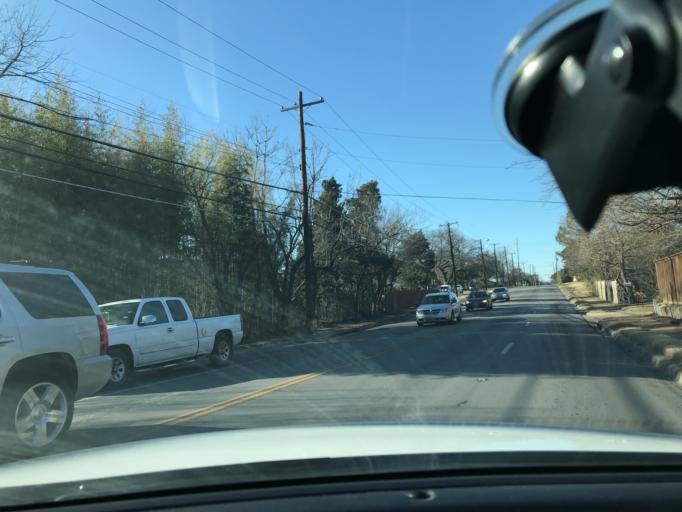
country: US
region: Texas
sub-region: Dallas County
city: Garland
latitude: 32.8302
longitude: -96.6868
